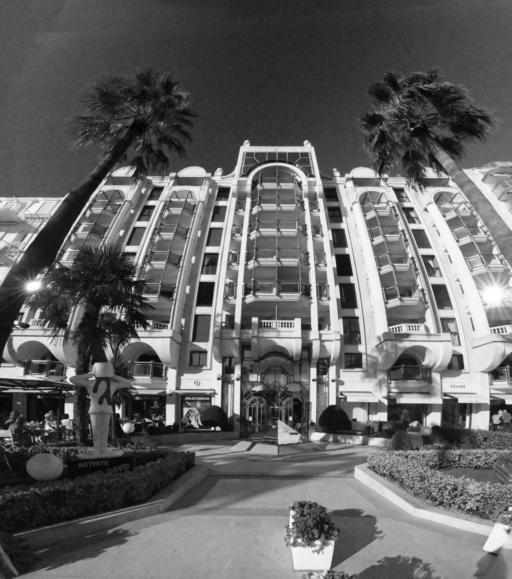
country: FR
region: Provence-Alpes-Cote d'Azur
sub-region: Departement des Alpes-Maritimes
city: Cannes
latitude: 43.5504
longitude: 7.0234
